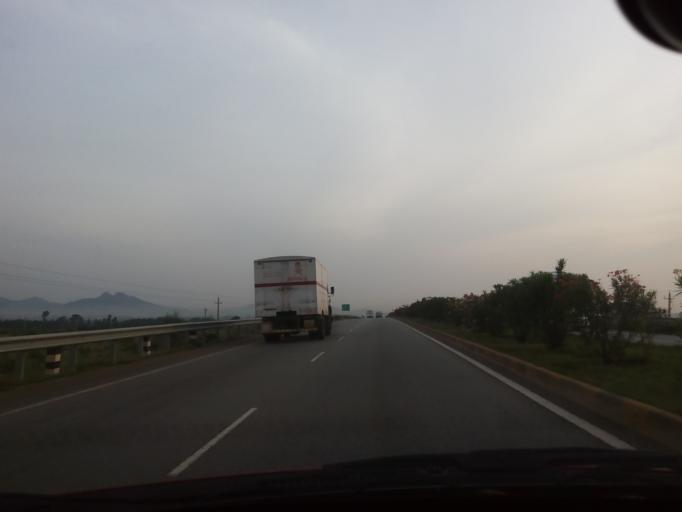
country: IN
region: Karnataka
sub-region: Chikkaballapur
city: Chik Ballapur
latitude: 13.4054
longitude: 77.7427
